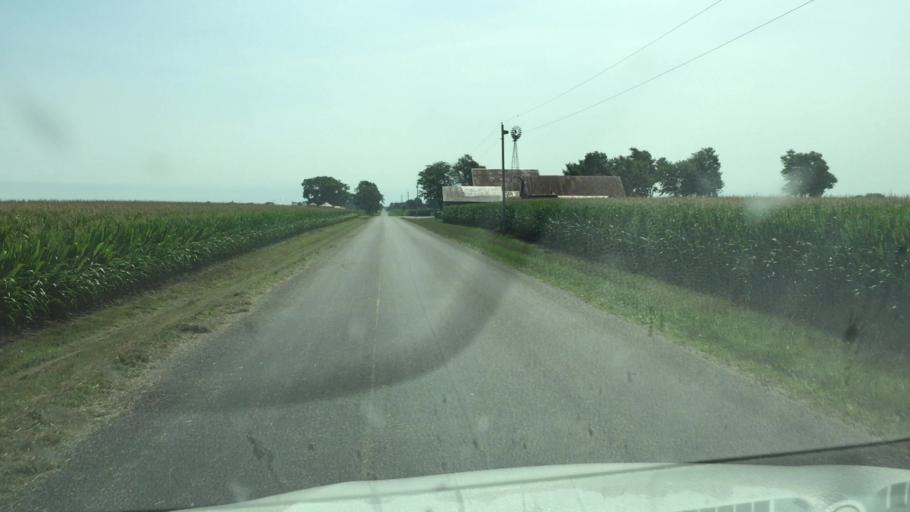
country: US
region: Illinois
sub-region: Hancock County
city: Nauvoo
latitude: 40.5073
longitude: -91.3120
